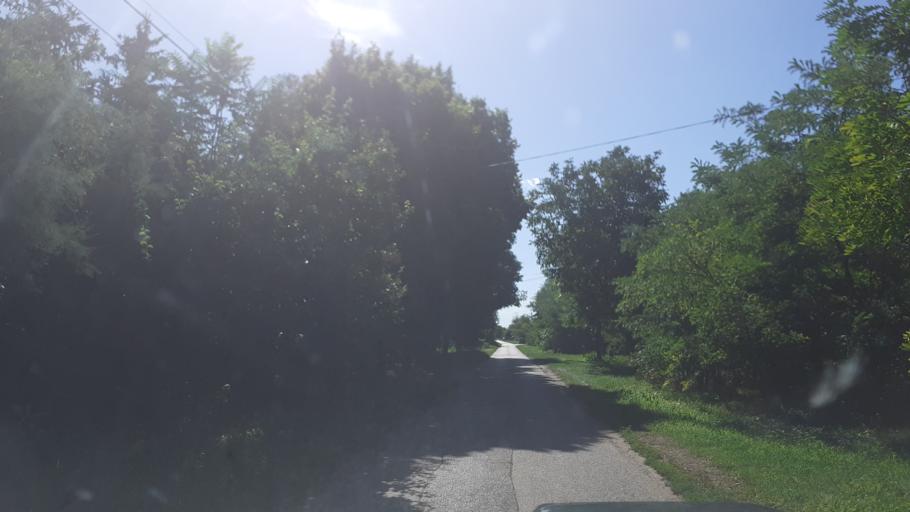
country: HU
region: Fejer
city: Baracska
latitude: 47.2802
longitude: 18.7729
